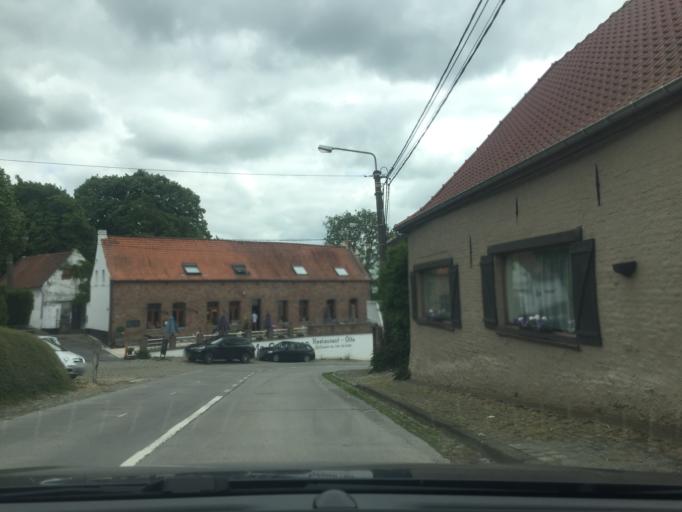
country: BE
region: Wallonia
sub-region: Province du Hainaut
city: Tournai
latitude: 50.6549
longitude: 3.4036
